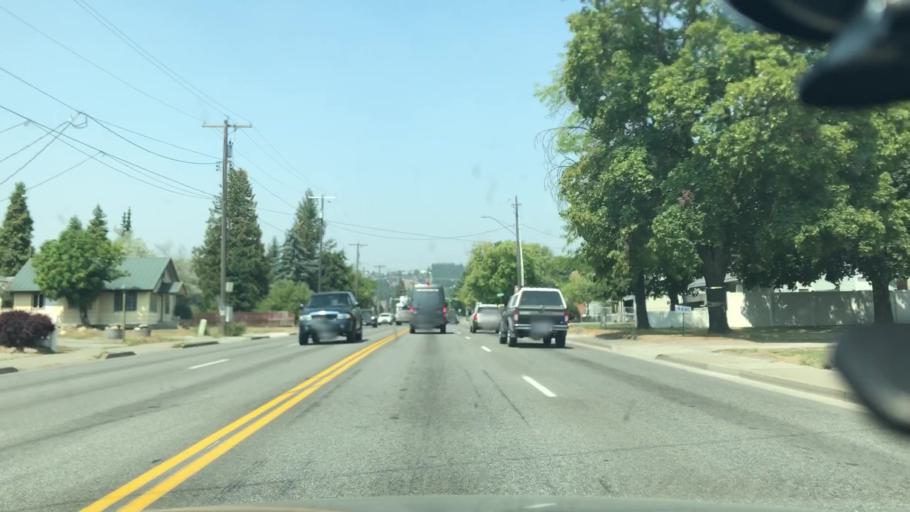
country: US
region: Washington
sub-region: Spokane County
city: Millwood
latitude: 47.6947
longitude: -117.2828
